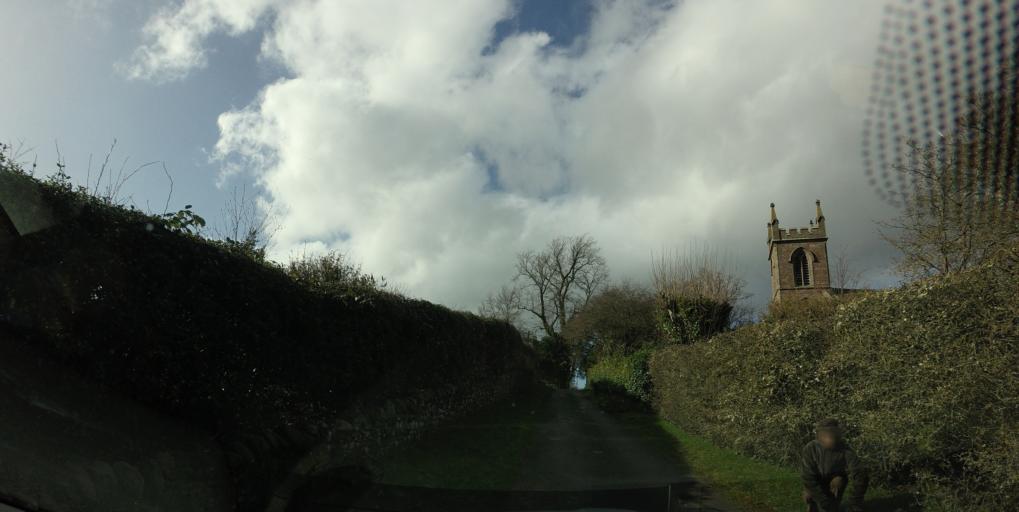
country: GB
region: Scotland
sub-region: Perth and Kinross
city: Bridge of Earn
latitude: 56.3273
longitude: -3.3905
